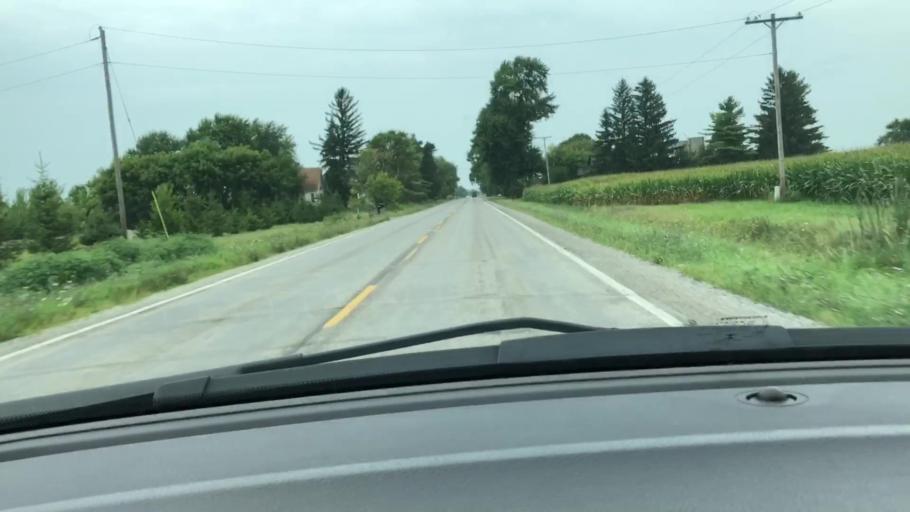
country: US
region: Michigan
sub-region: Saginaw County
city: Freeland
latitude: 43.5571
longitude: -84.0899
